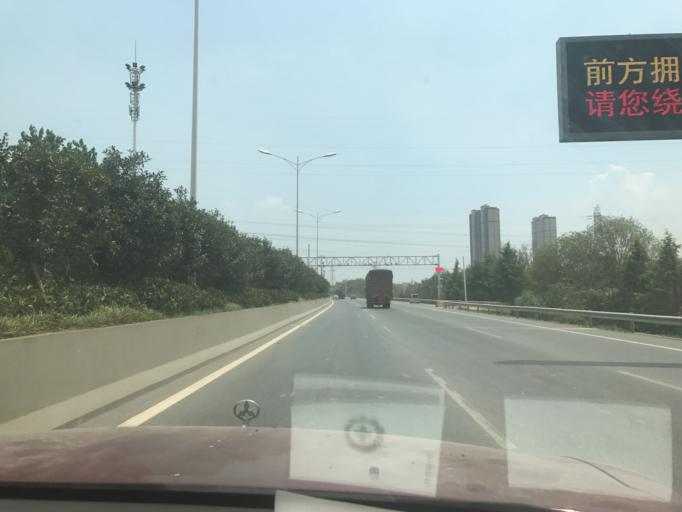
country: CN
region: Hubei
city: Houhu
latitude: 30.6722
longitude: 114.3062
